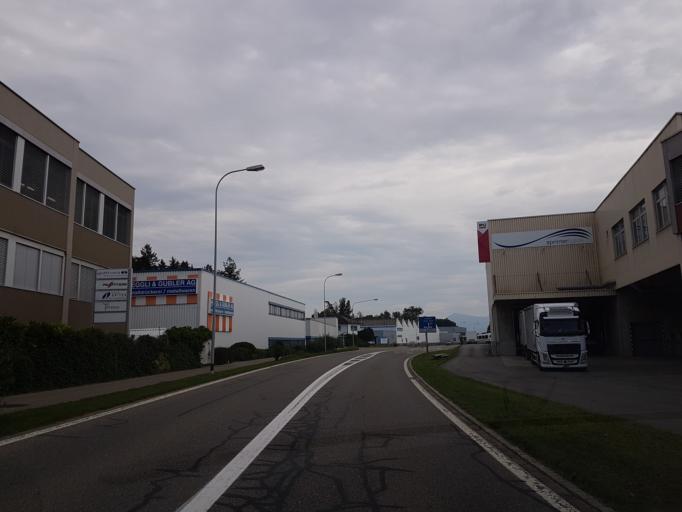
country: CH
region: Aargau
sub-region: Bezirk Muri
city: Muri
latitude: 47.2634
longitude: 8.3517
